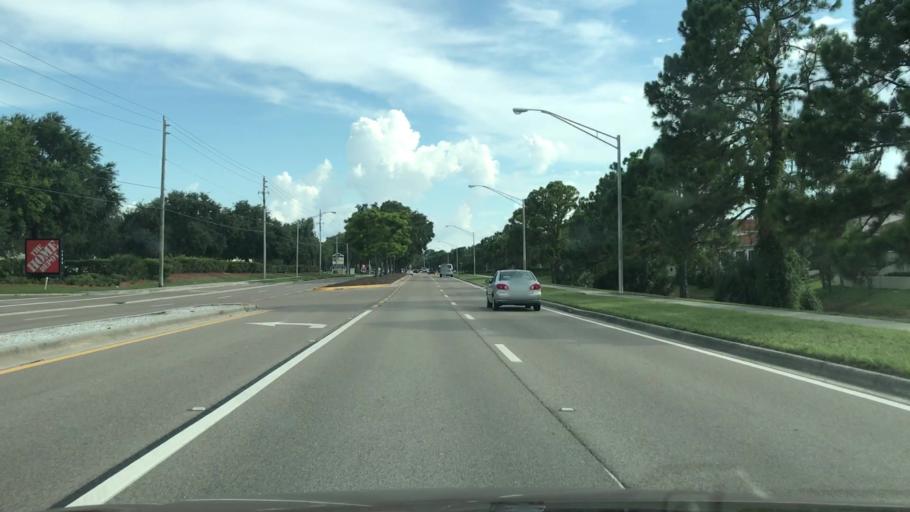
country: US
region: Florida
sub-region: Sarasota County
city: Venice Gardens
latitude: 27.0538
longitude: -82.3959
